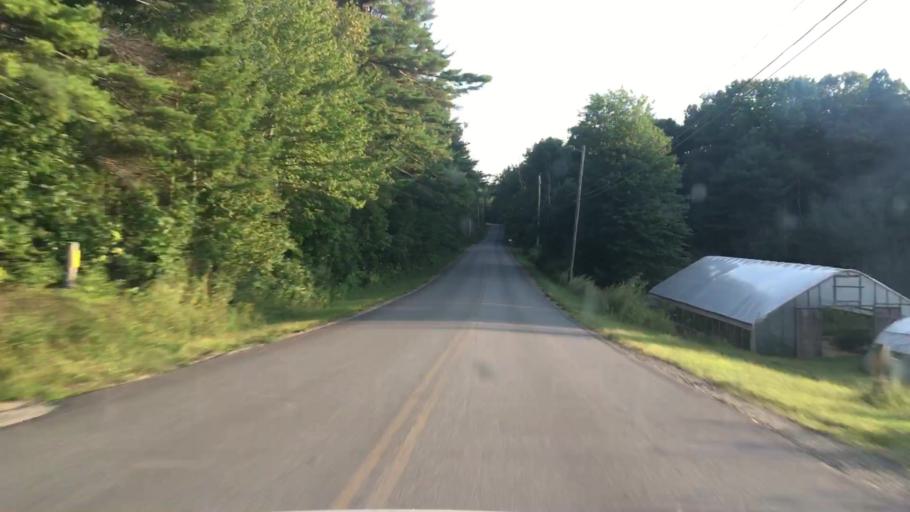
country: US
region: Maine
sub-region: Penobscot County
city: Hampden
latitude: 44.7093
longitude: -68.8878
